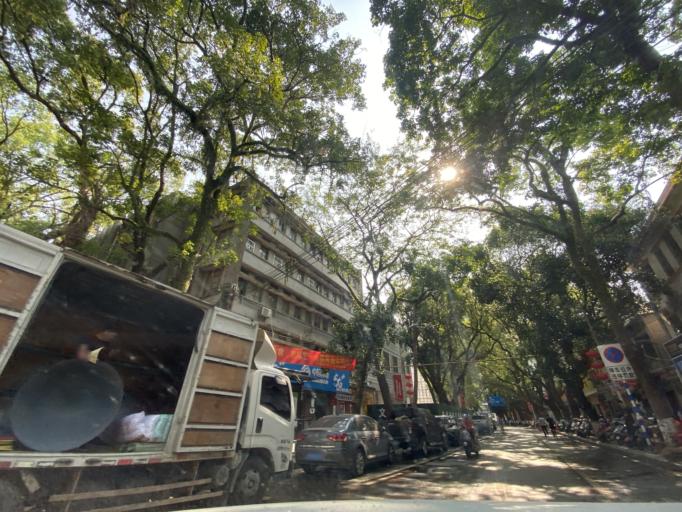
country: CN
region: Hainan
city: Chongshan
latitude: 18.7801
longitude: 109.5118
